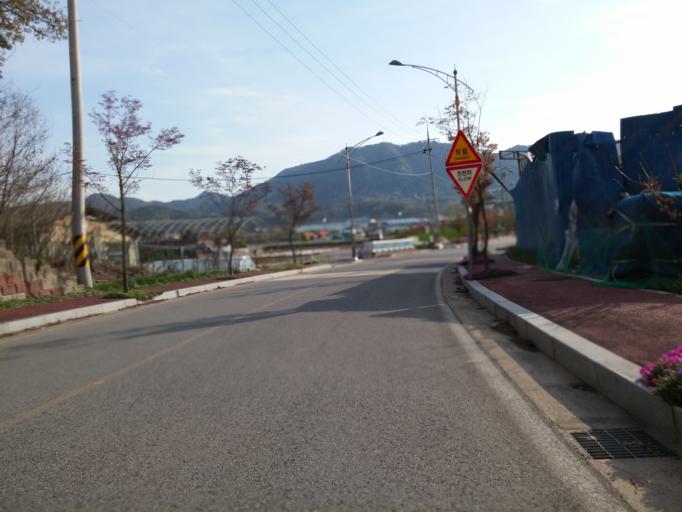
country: KR
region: Chungcheongbuk-do
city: Okcheon
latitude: 36.2723
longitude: 127.5887
